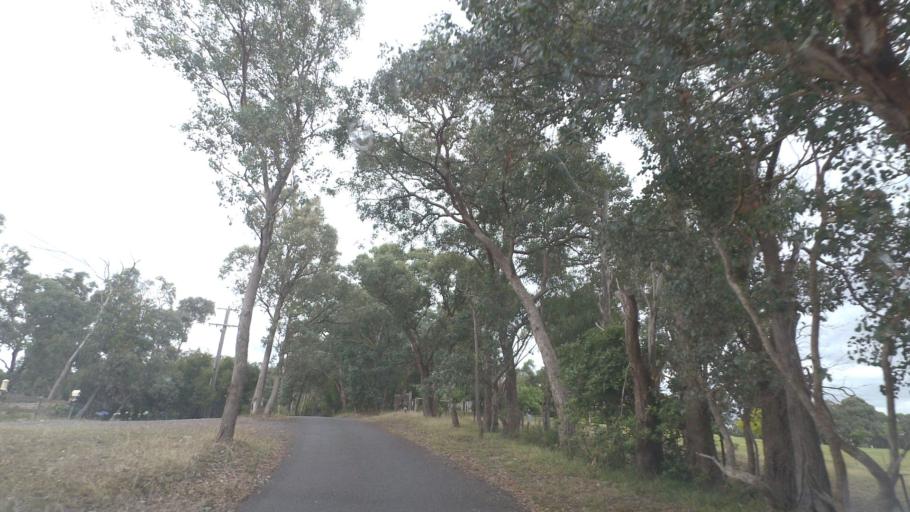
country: AU
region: Victoria
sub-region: Manningham
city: Warrandyte
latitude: -37.7565
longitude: 145.2149
